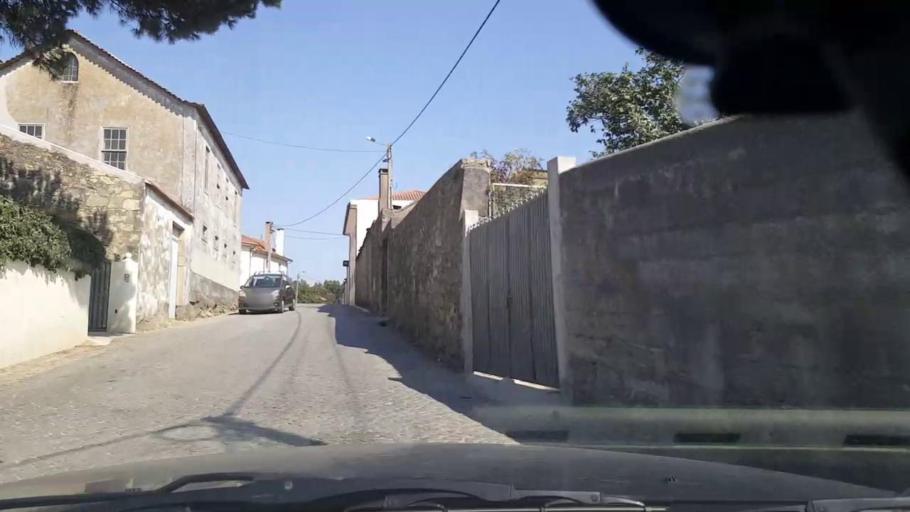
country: PT
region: Porto
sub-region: Povoa de Varzim
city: Pedroso
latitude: 41.4012
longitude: -8.6854
